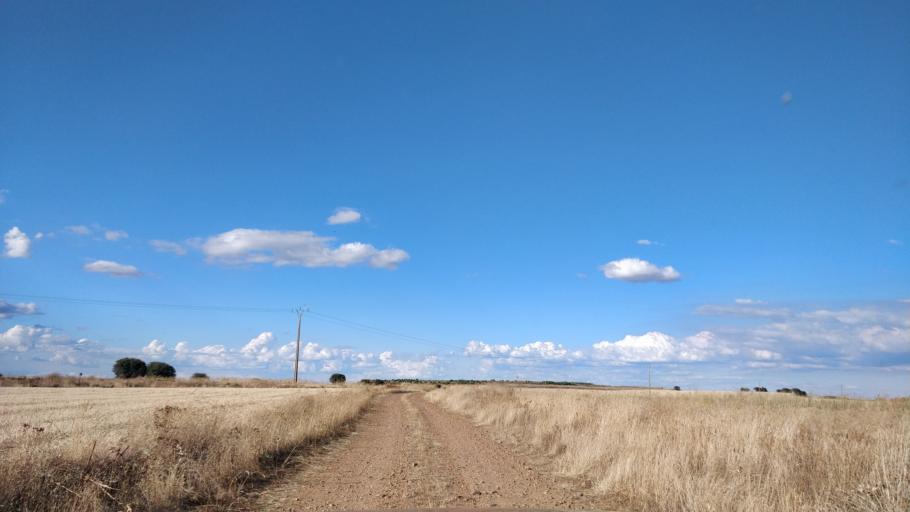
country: ES
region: Castille and Leon
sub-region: Provincia de Leon
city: Santa Cristina de Valmadrigal
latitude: 42.3392
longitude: -5.2735
